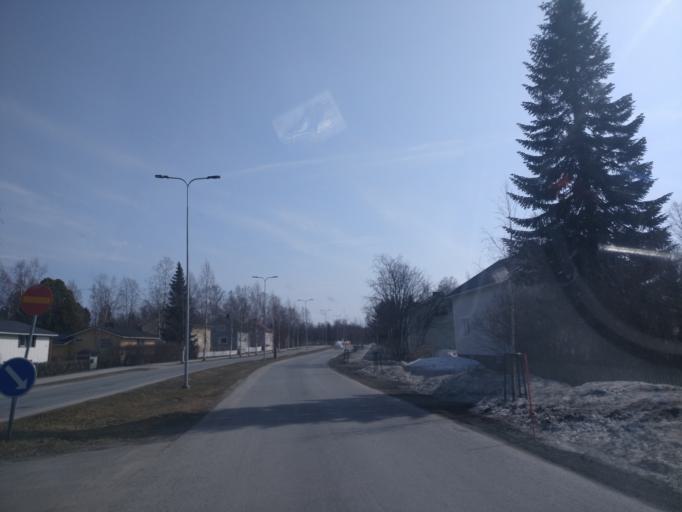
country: FI
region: Lapland
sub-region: Kemi-Tornio
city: Kemi
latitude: 65.7286
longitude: 24.6088
